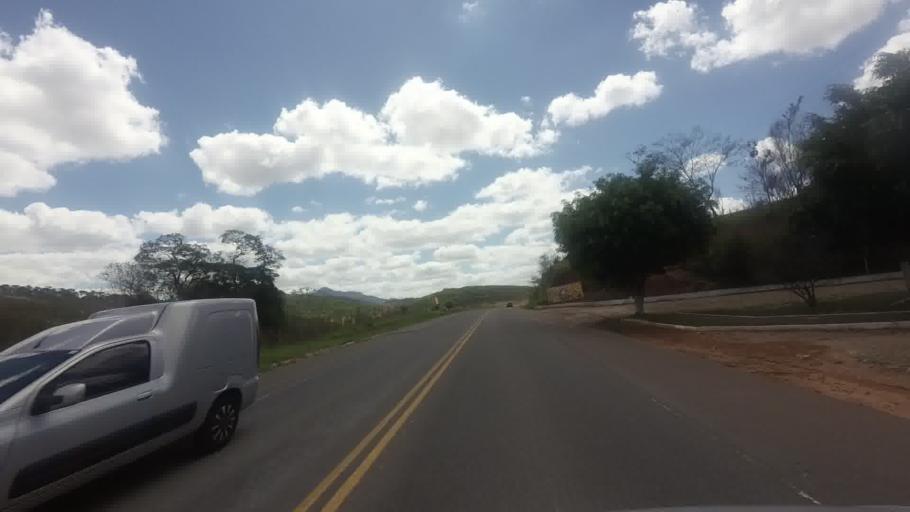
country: BR
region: Minas Gerais
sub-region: Recreio
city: Recreio
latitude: -21.6618
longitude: -42.3772
